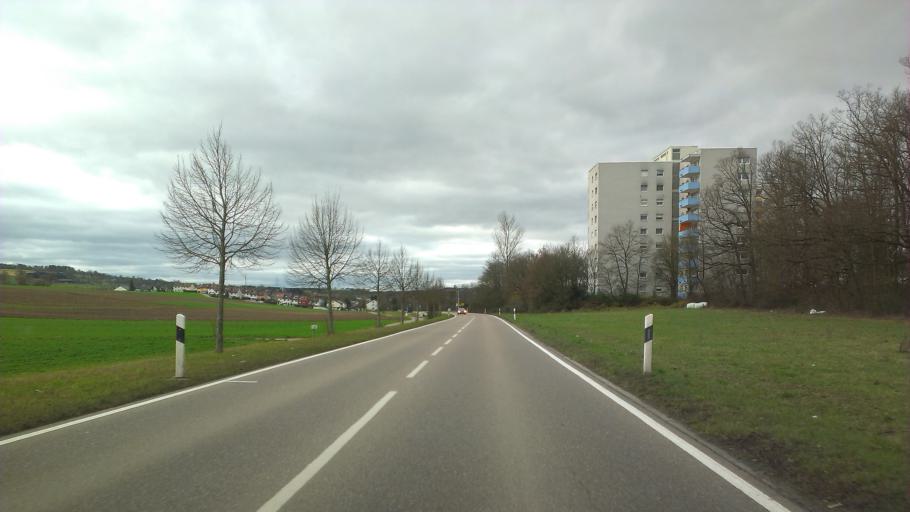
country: DE
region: Baden-Wuerttemberg
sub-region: Karlsruhe Region
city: Illingen
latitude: 48.9525
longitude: 8.9409
